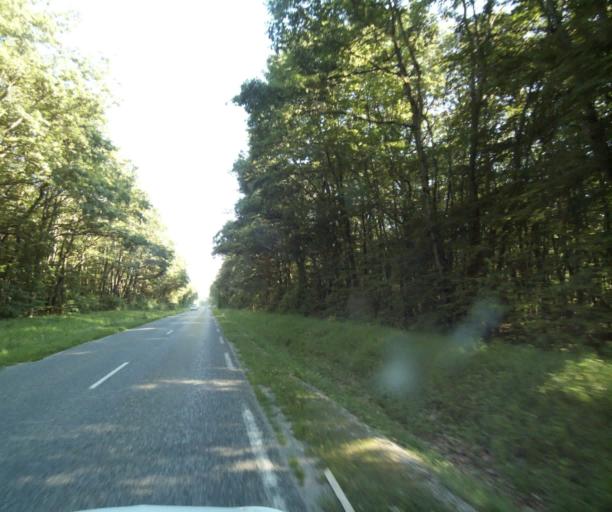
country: FR
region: Rhone-Alpes
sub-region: Departement de la Haute-Savoie
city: Messery
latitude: 46.3292
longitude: 6.2922
